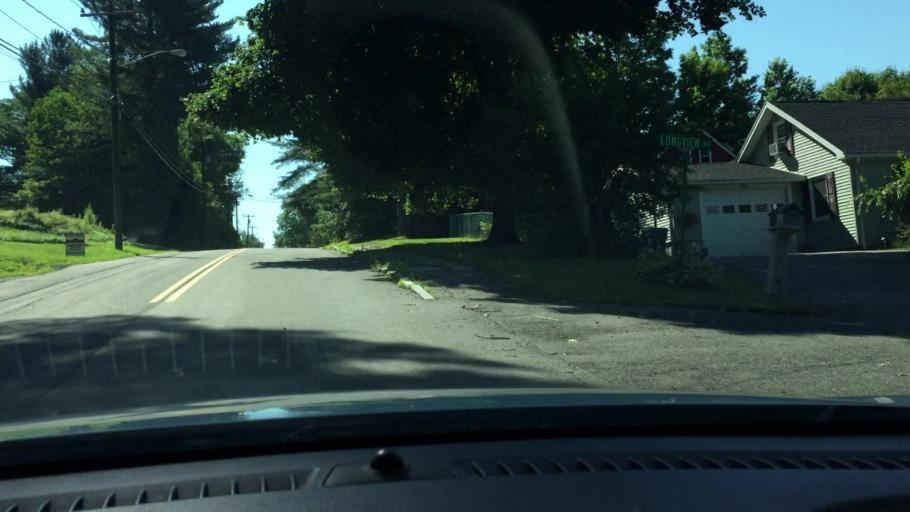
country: US
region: Massachusetts
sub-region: Berkshire County
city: Lanesborough
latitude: 42.5160
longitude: -73.2248
